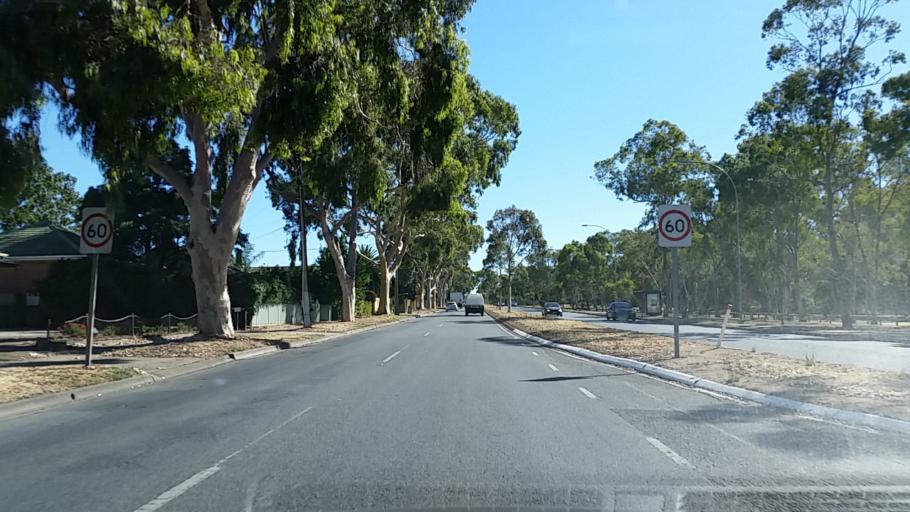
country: AU
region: South Australia
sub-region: Salisbury
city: Ingle Farm
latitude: -34.8114
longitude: 138.6451
